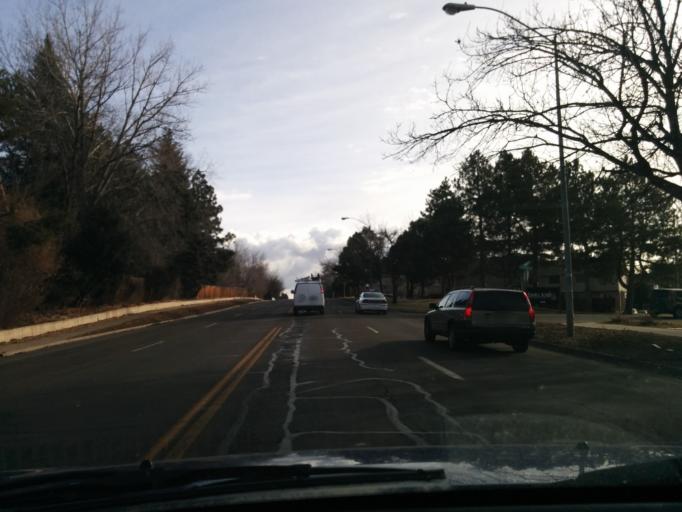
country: US
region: Colorado
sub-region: Larimer County
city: Fort Collins
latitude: 40.5670
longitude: -105.0513
